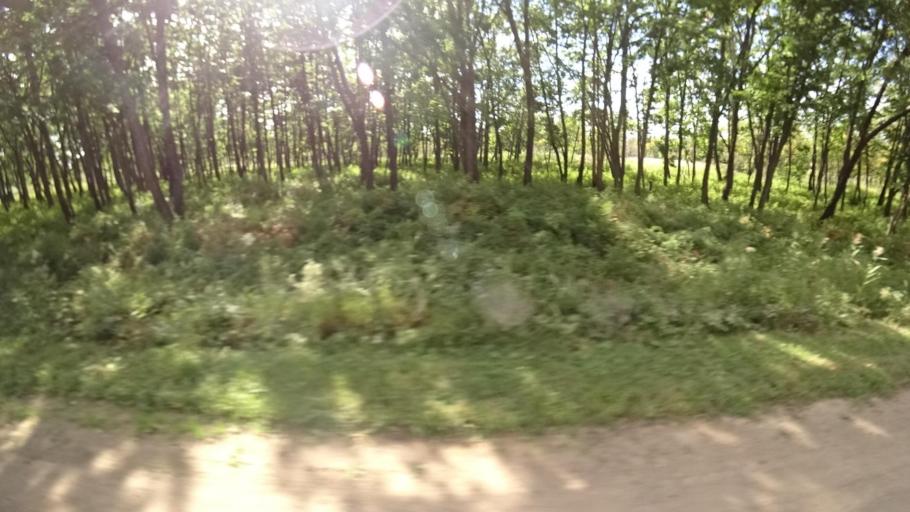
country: RU
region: Primorskiy
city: Yakovlevka
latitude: 44.3826
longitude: 133.5353
